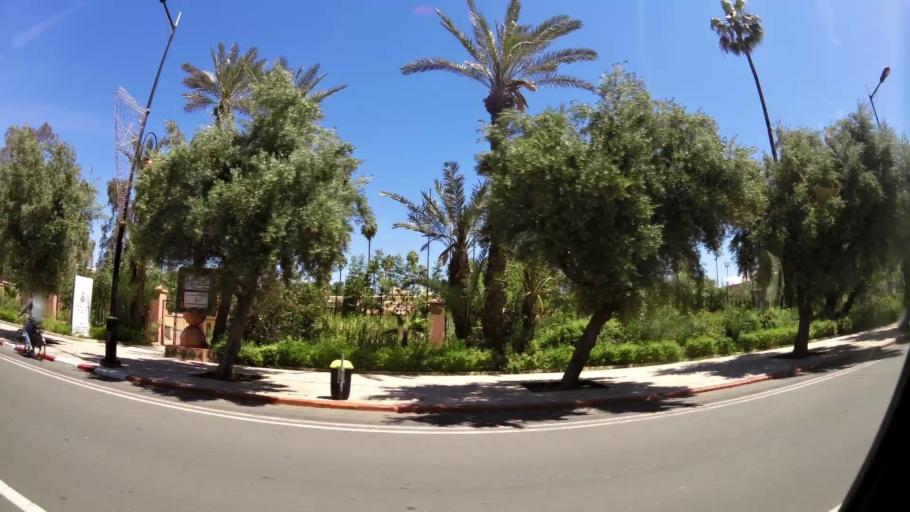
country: MA
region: Marrakech-Tensift-Al Haouz
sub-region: Marrakech
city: Marrakesh
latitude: 31.6286
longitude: -8.0115
